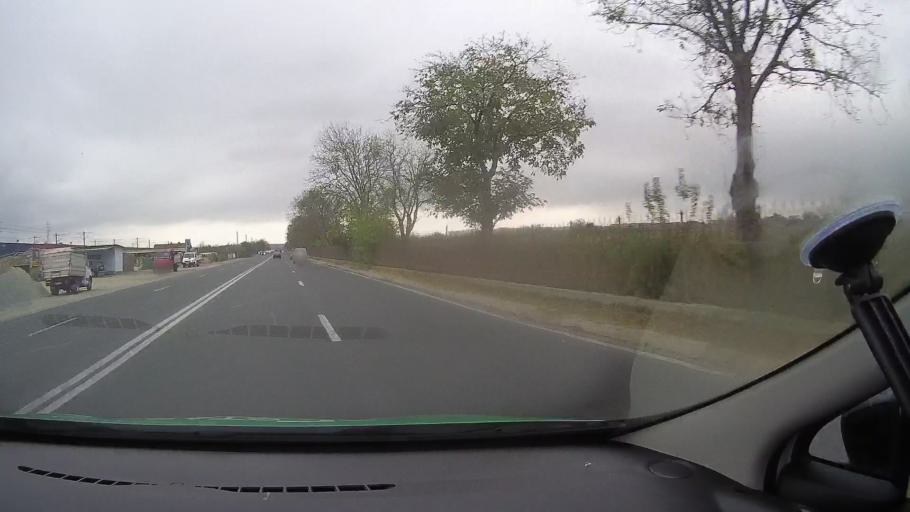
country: RO
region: Constanta
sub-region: Oras Murfatlar
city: Murfatlar
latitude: 44.1713
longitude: 28.4255
